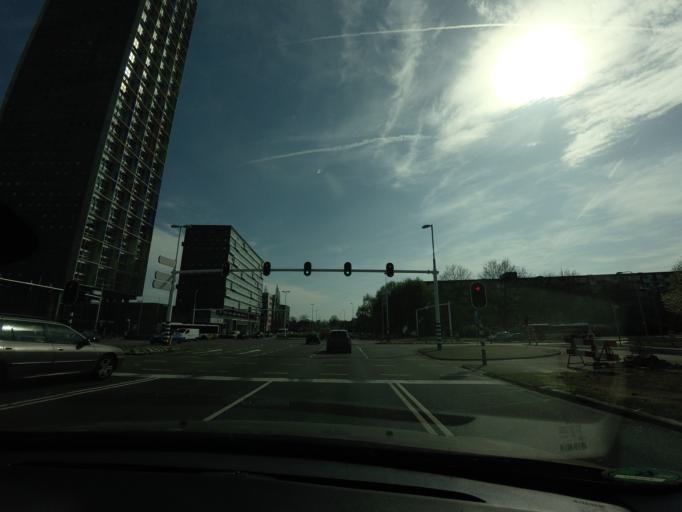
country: NL
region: North Brabant
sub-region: Gemeente Tilburg
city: Tilburg
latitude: 51.5610
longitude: 5.0646
